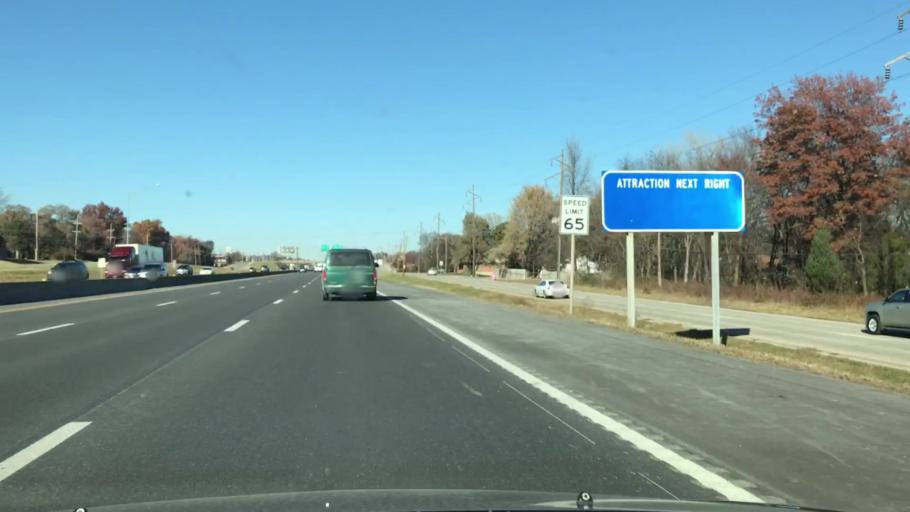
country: US
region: Missouri
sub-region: Jackson County
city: Grandview
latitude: 38.8643
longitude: -94.5267
